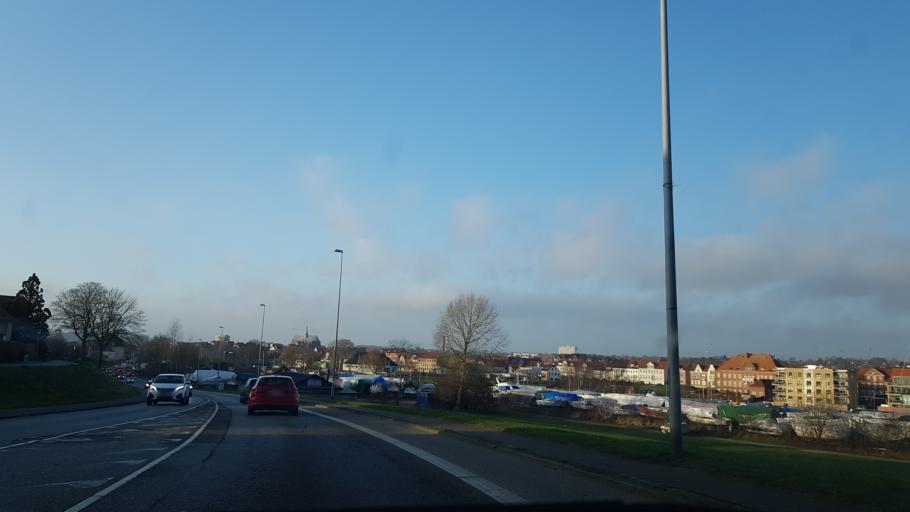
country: DK
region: South Denmark
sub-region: Haderslev Kommune
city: Haderslev
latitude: 55.2466
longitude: 9.5013
